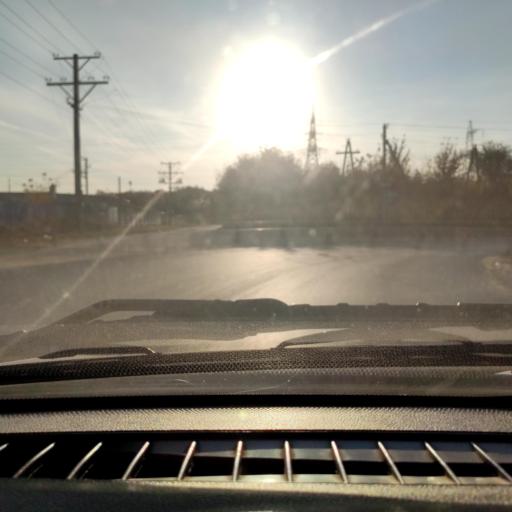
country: RU
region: Samara
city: Zhigulevsk
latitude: 53.5243
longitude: 49.4877
